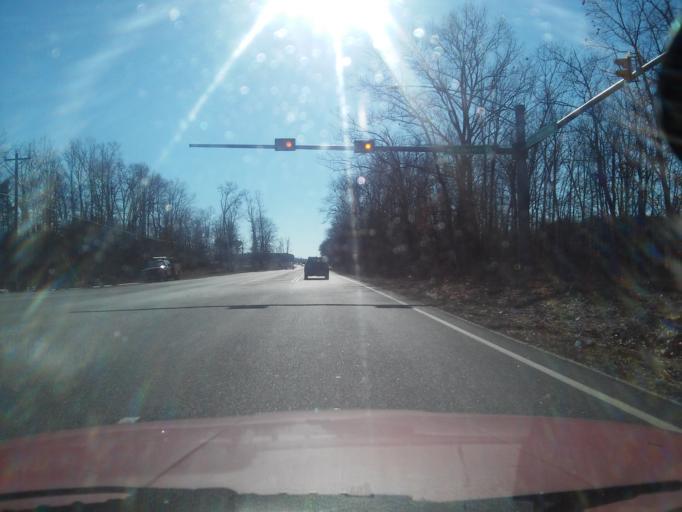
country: US
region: Virginia
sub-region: Fluvanna County
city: Palmyra
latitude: 37.9866
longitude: -78.2055
